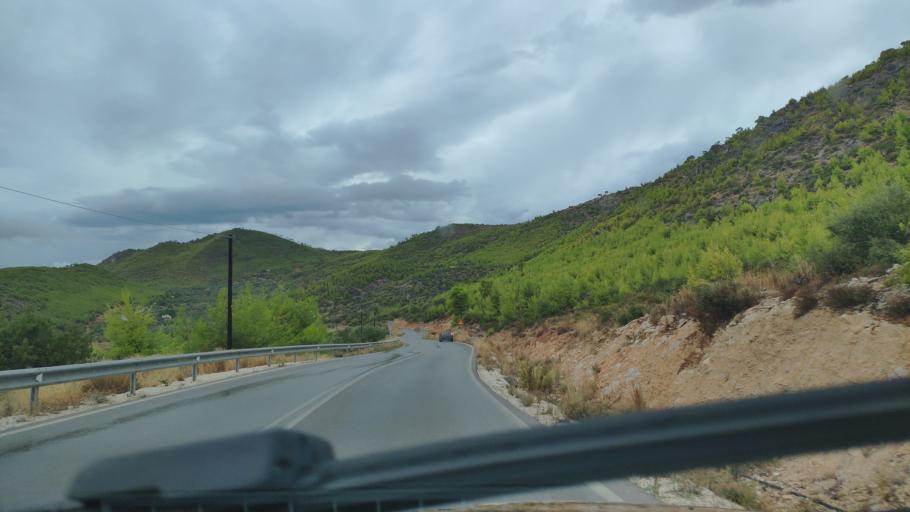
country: GR
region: Peloponnese
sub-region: Nomos Korinthias
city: Perachora
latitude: 38.0314
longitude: 22.9276
